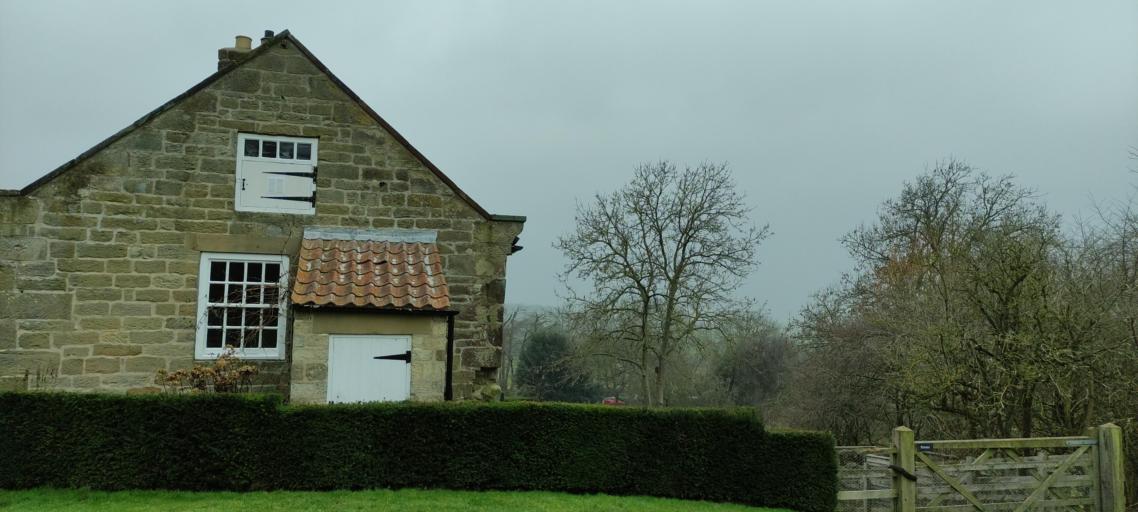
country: GB
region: England
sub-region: North Yorkshire
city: Northallerton
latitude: 54.3804
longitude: -1.3105
